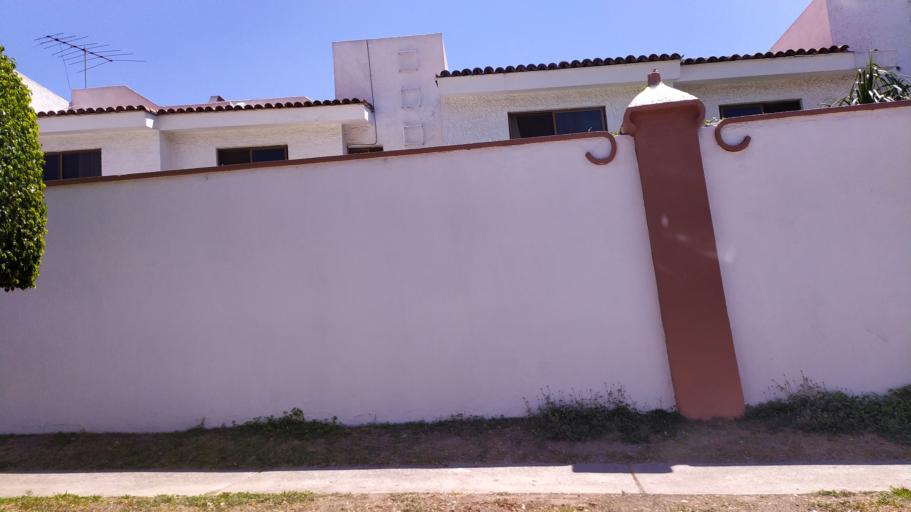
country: MX
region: Jalisco
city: Zapopan2
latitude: 20.6920
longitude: -103.4344
